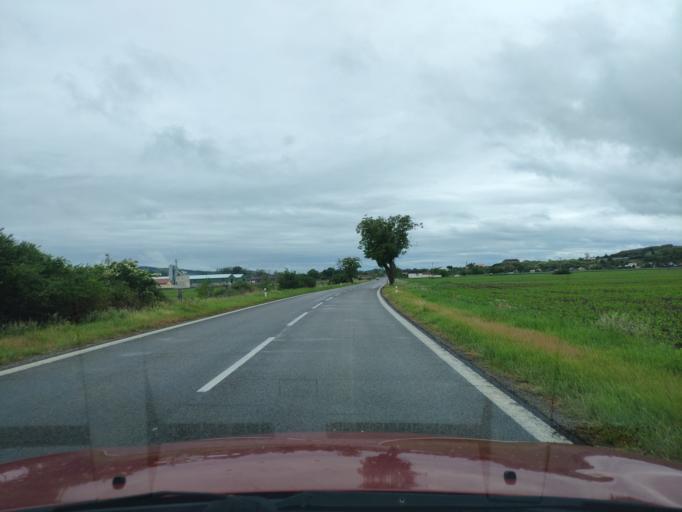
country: HU
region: Borsod-Abauj-Zemplen
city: Karcsa
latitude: 48.4099
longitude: 21.8215
